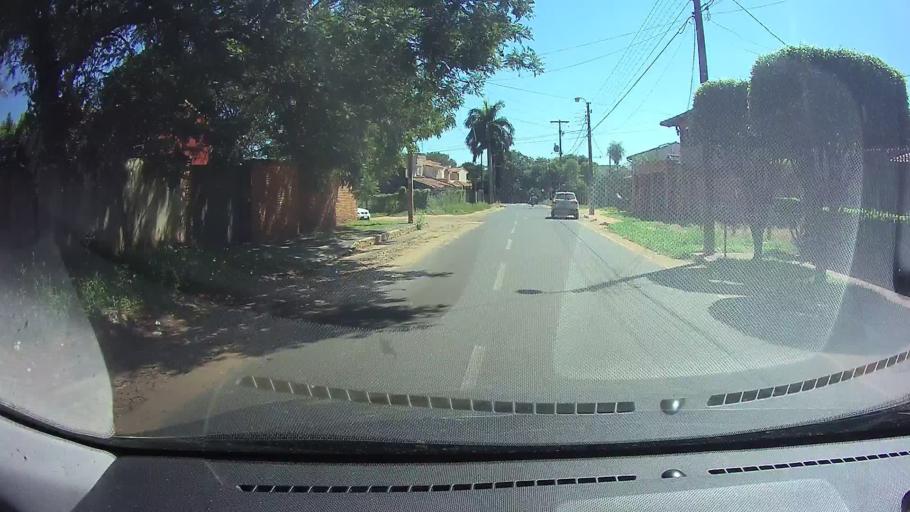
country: PY
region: Central
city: Fernando de la Mora
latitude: -25.3242
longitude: -57.5286
